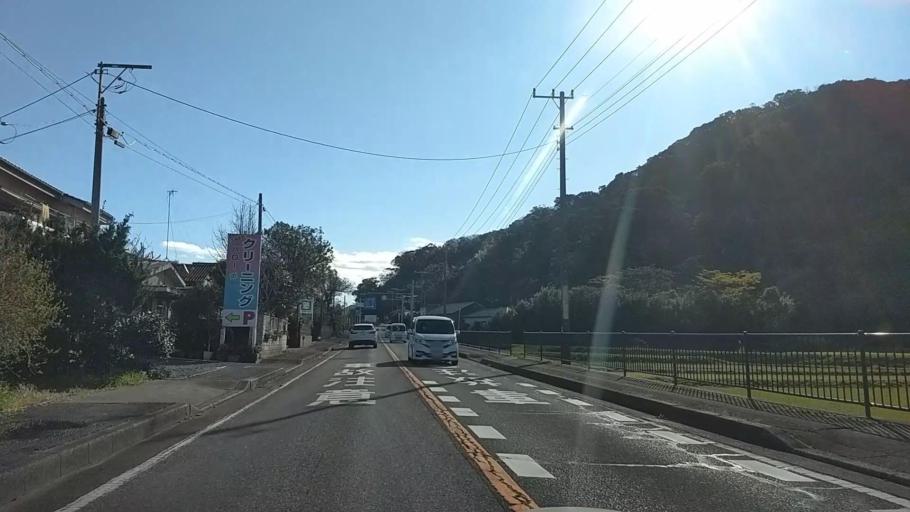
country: JP
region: Chiba
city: Tateyama
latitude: 35.1034
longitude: 139.8444
